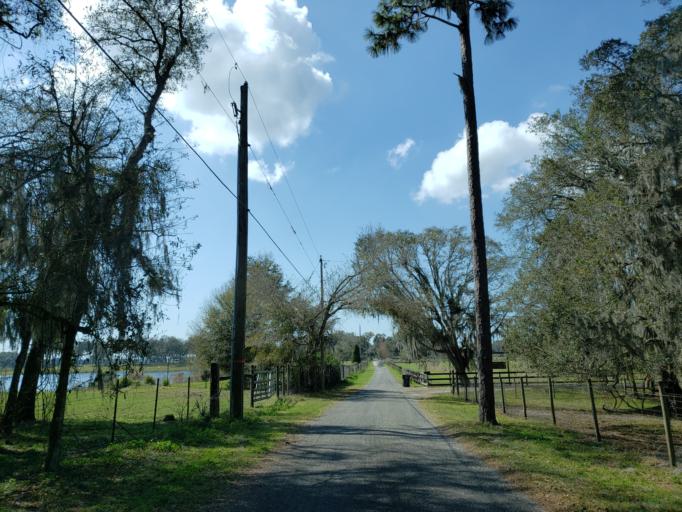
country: US
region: Florida
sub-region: Hillsborough County
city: Keystone
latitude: 28.1514
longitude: -82.6426
